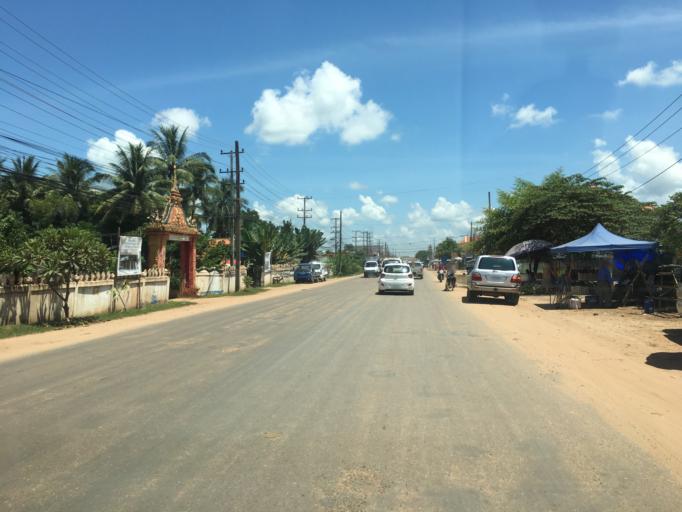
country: TH
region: Nong Khai
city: Si Chiang Mai
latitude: 18.0151
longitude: 102.5461
